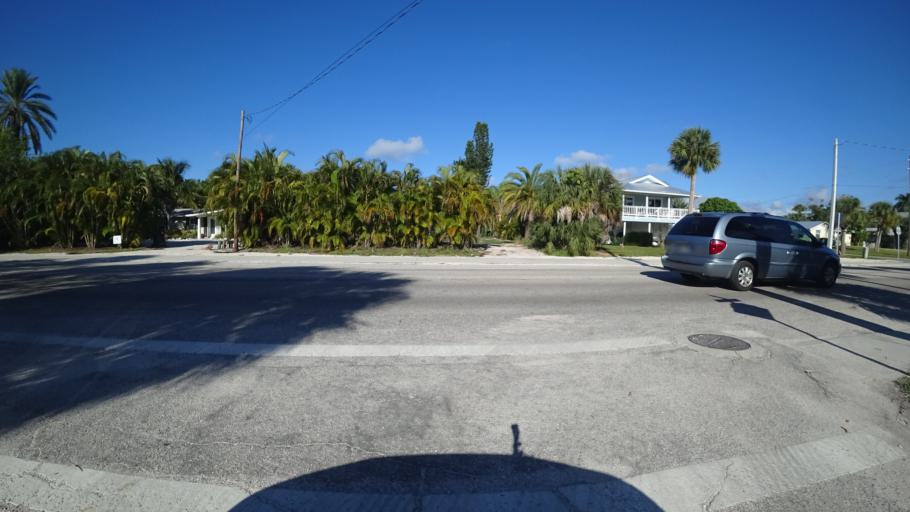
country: US
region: Florida
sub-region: Manatee County
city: Anna Maria
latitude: 27.5239
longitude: -82.7323
